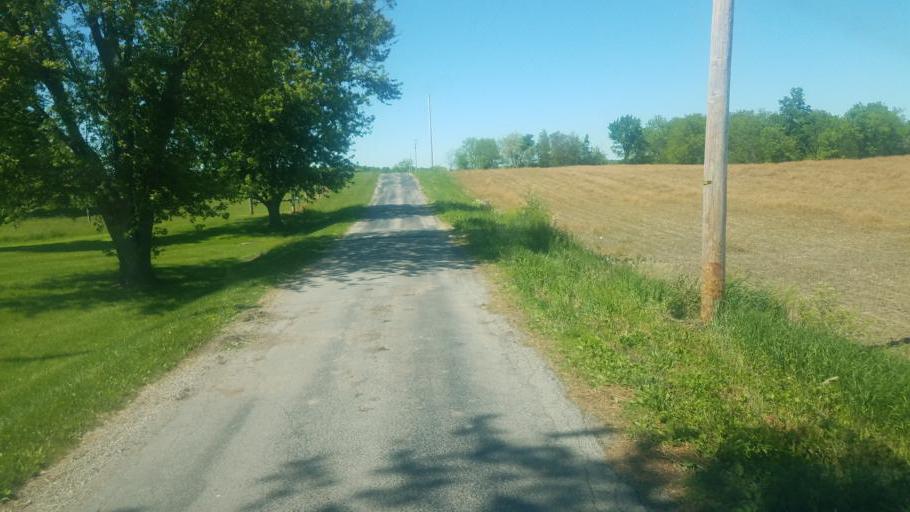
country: US
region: Ohio
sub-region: Logan County
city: De Graff
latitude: 40.2905
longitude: -83.8527
